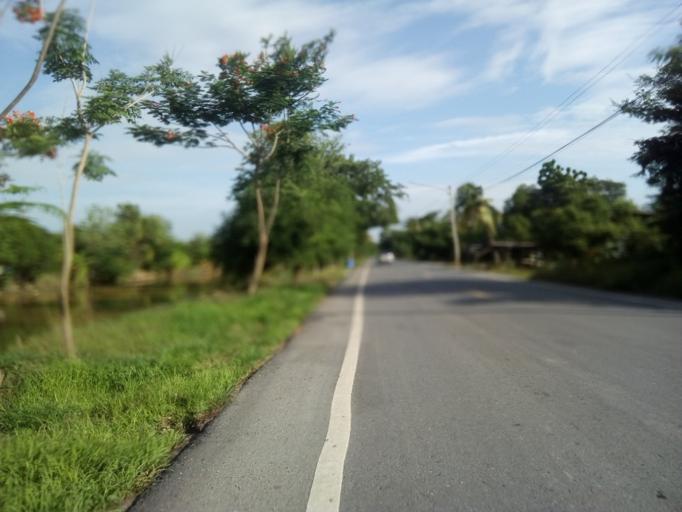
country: TH
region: Pathum Thani
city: Nong Suea
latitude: 14.1129
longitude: 100.8461
